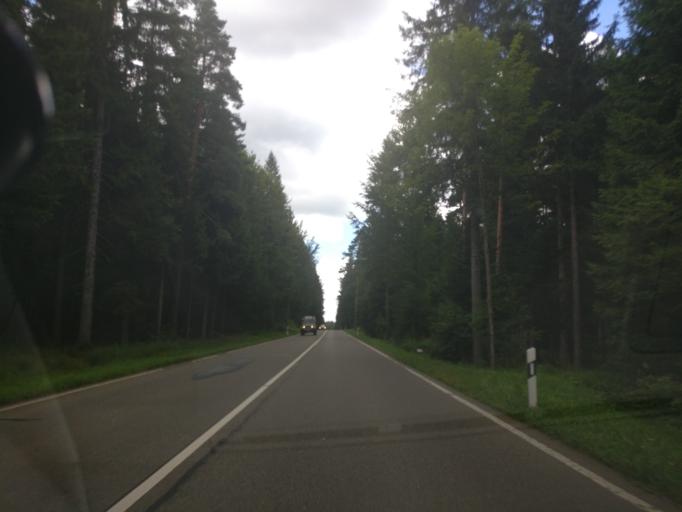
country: DE
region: Baden-Wuerttemberg
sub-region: Karlsruhe Region
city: Baiersbronn
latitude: 48.5374
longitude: 8.4292
